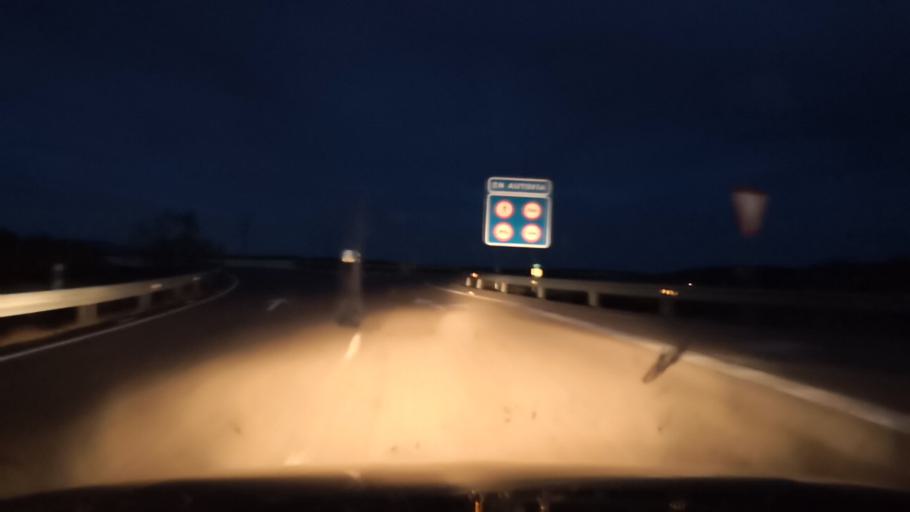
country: ES
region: Extremadura
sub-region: Provincia de Caceres
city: Plasencia
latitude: 39.9799
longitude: -6.1524
